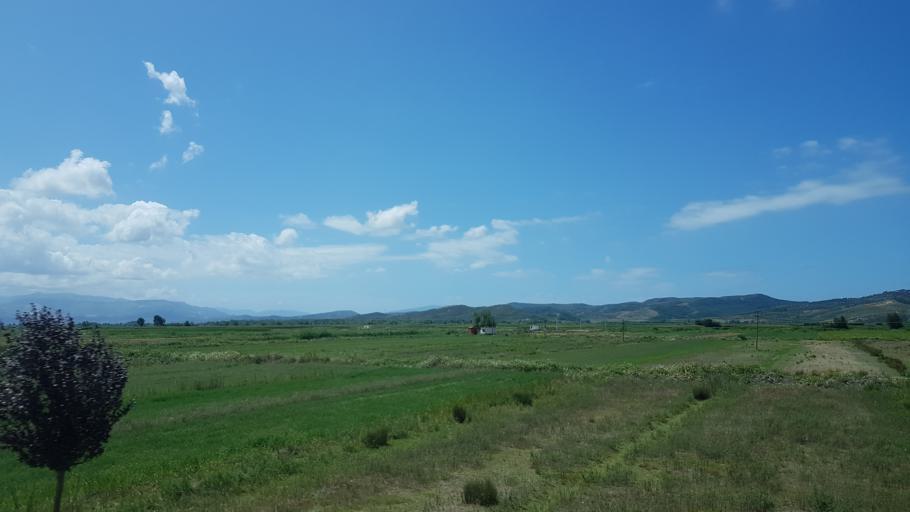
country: AL
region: Fier
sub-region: Rrethi i Fierit
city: Cakran
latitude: 40.5961
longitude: 19.5702
